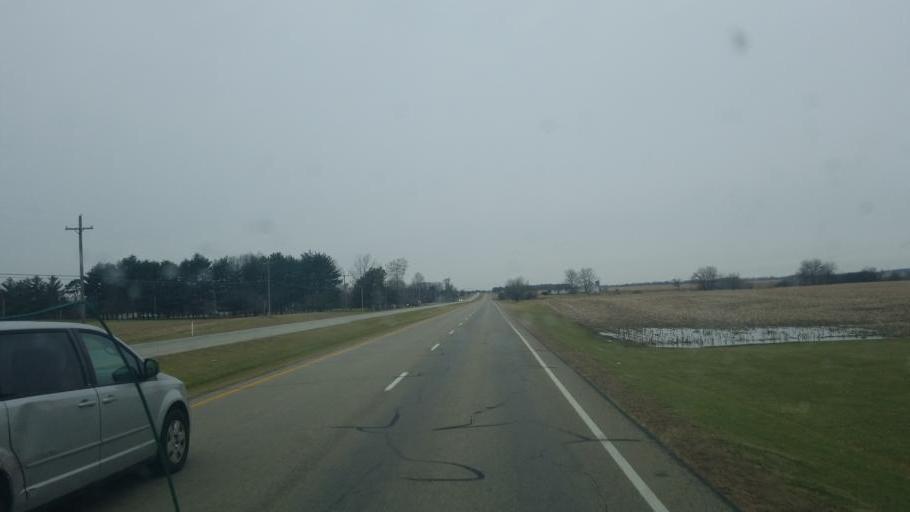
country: US
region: Indiana
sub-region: Henry County
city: Knightstown
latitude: 39.7934
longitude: -85.5614
